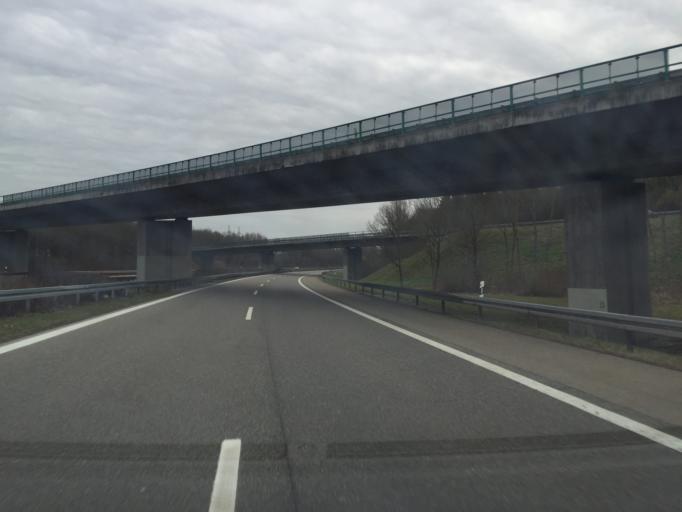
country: DE
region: Baden-Wuerttemberg
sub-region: Freiburg Region
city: Volkertshausen
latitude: 47.8105
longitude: 8.8542
